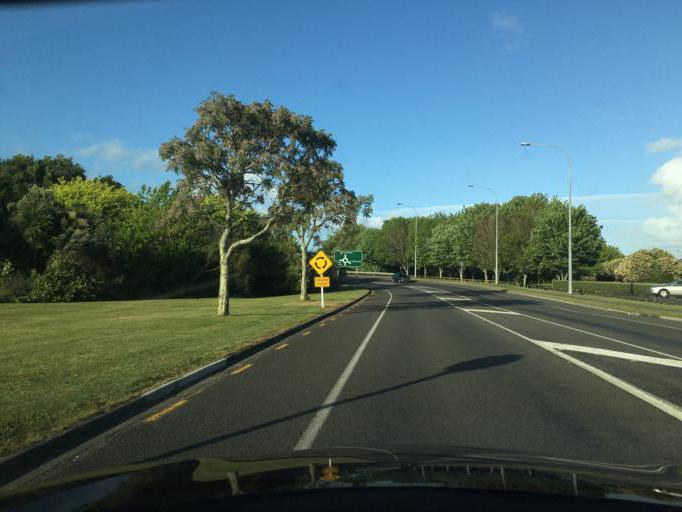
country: NZ
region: Waikato
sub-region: Waipa District
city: Cambridge
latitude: -38.0091
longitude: 175.3298
